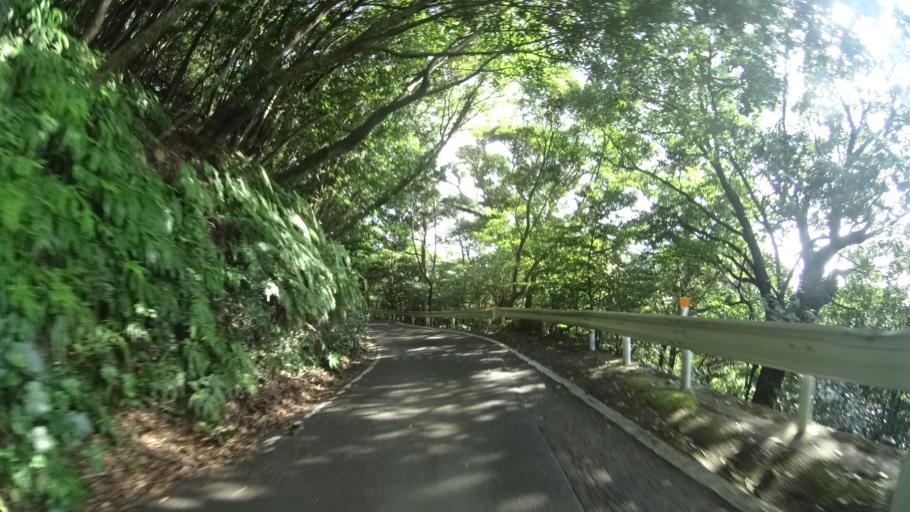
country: JP
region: Kagoshima
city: Nishinoomote
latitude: 30.3382
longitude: 130.3962
